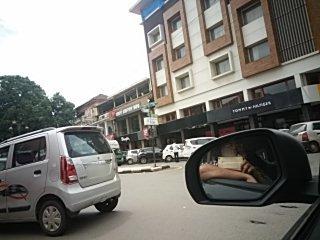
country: IN
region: Goa
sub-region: North Goa
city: Panaji
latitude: 15.5005
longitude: 73.8281
